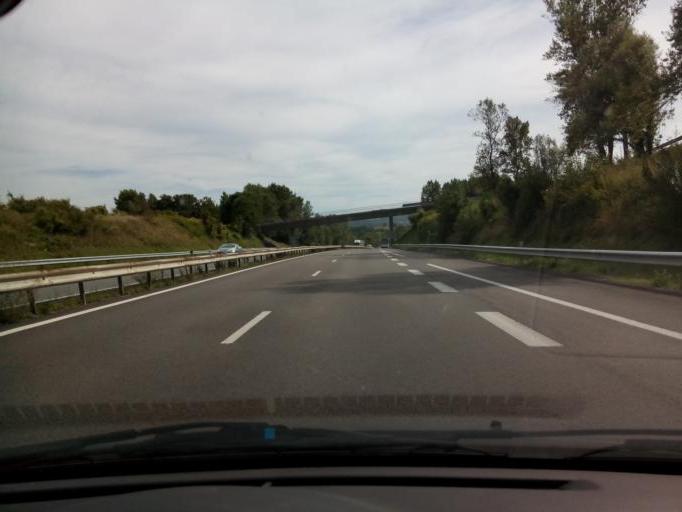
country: FR
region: Rhone-Alpes
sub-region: Departement de l'Isere
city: Saint-Victor-de-Cessieu
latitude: 45.5264
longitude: 5.4102
